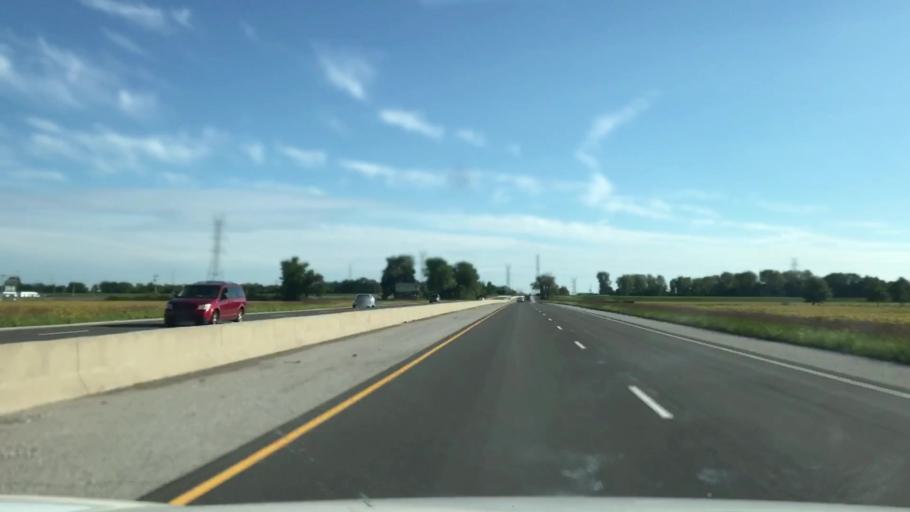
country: US
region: Illinois
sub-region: Madison County
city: Hartford
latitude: 38.8121
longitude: -90.0987
